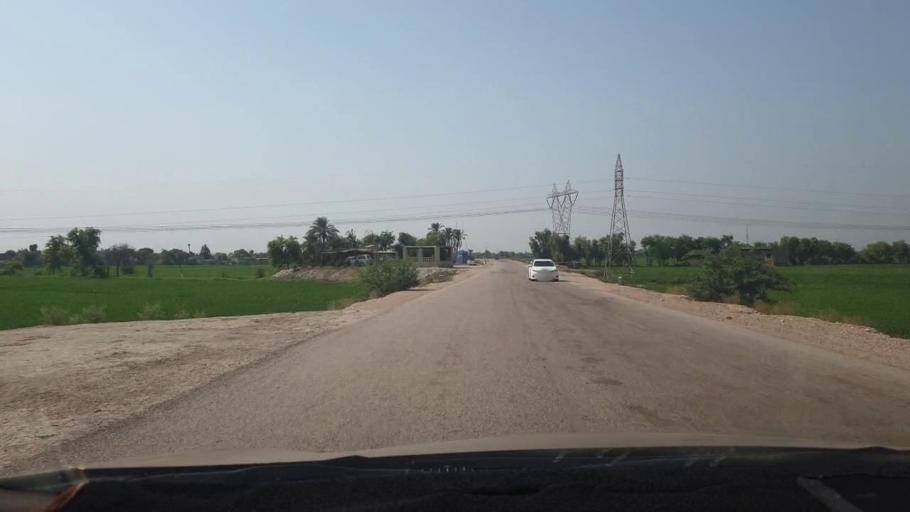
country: PK
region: Sindh
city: Larkana
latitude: 27.6064
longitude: 68.2406
